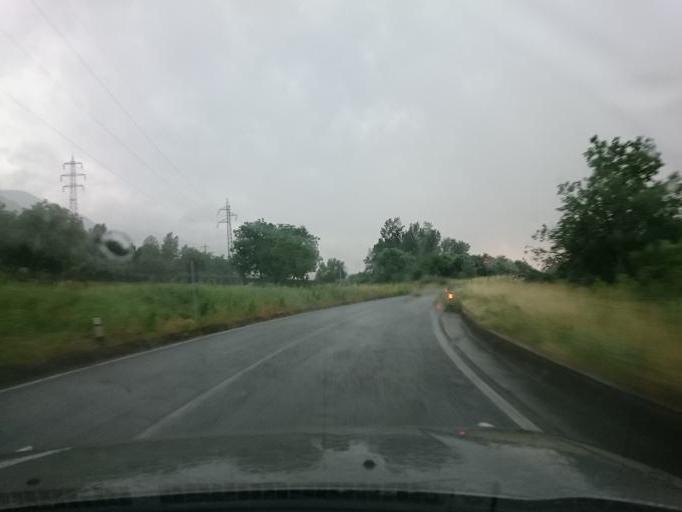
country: IT
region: Lombardy
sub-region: Provincia di Brescia
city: Ceto
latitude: 46.0136
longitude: 10.3501
